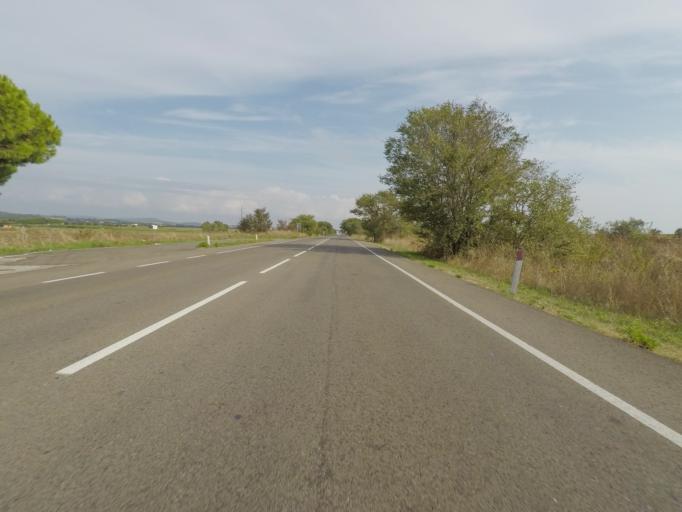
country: IT
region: Tuscany
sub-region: Provincia di Grosseto
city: Capalbio
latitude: 42.4149
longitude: 11.3911
